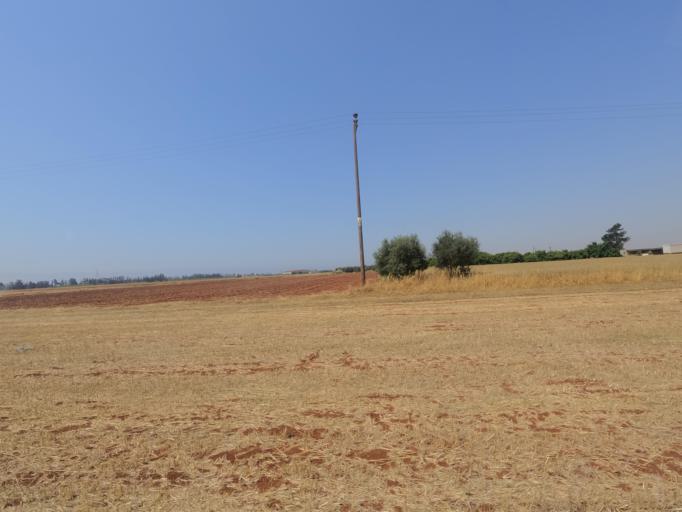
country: CY
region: Ammochostos
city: Avgorou
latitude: 35.0164
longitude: 33.8114
